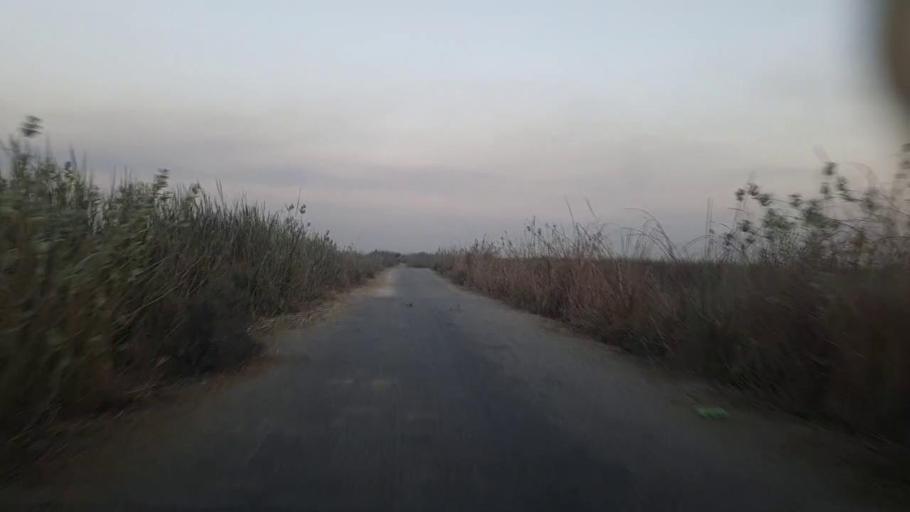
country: PK
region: Sindh
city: Kandiari
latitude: 26.6871
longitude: 68.9282
